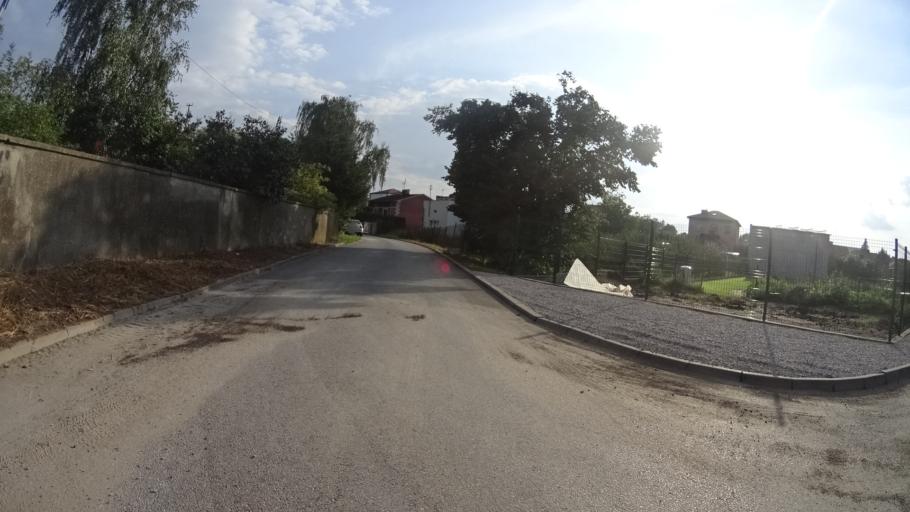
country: PL
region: Masovian Voivodeship
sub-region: Powiat grojecki
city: Mogielnica
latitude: 51.6895
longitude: 20.7263
